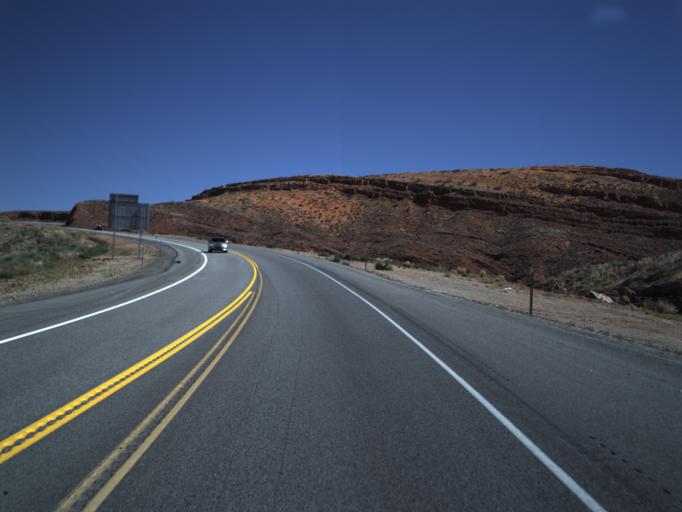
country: US
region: Utah
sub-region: Washington County
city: Washington
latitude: 37.1126
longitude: -113.4363
